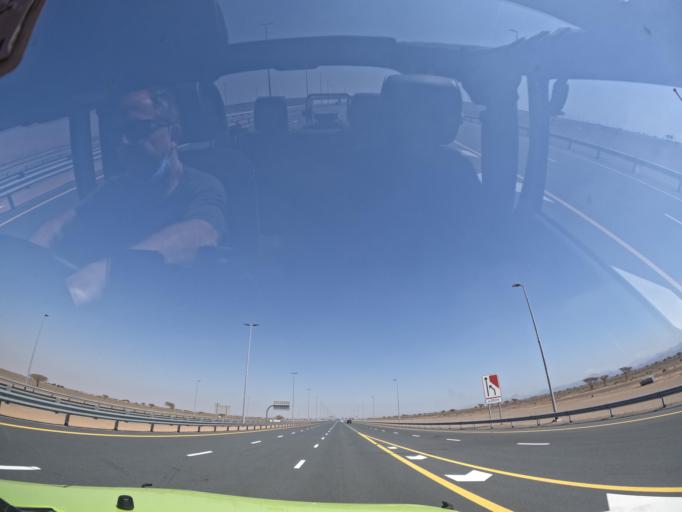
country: AE
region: Ash Shariqah
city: Adh Dhayd
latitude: 25.0753
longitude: 55.9116
